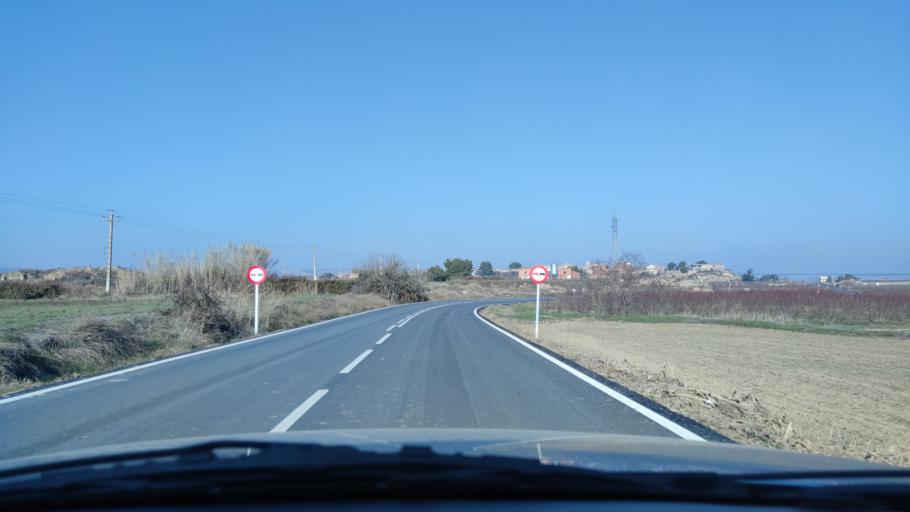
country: ES
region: Catalonia
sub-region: Provincia de Lleida
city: Torrefarrera
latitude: 41.7046
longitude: 0.6243
